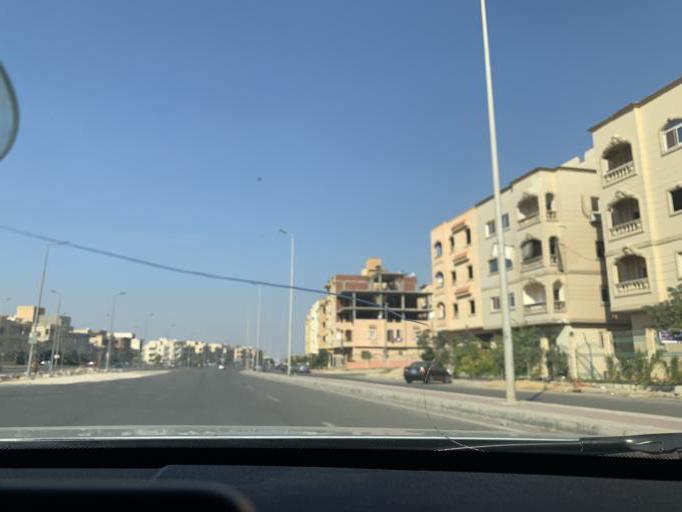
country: EG
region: Muhafazat al Qahirah
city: Cairo
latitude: 30.0025
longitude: 31.4689
